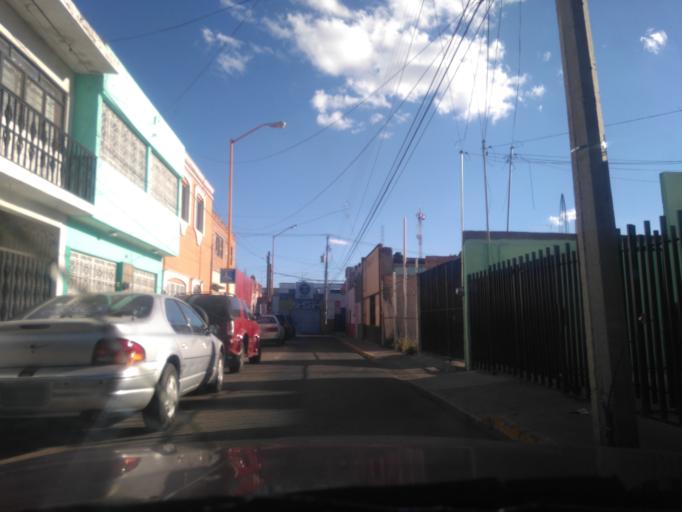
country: MX
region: Aguascalientes
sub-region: Aguascalientes
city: Aguascalientes
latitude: 21.8779
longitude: -102.3048
